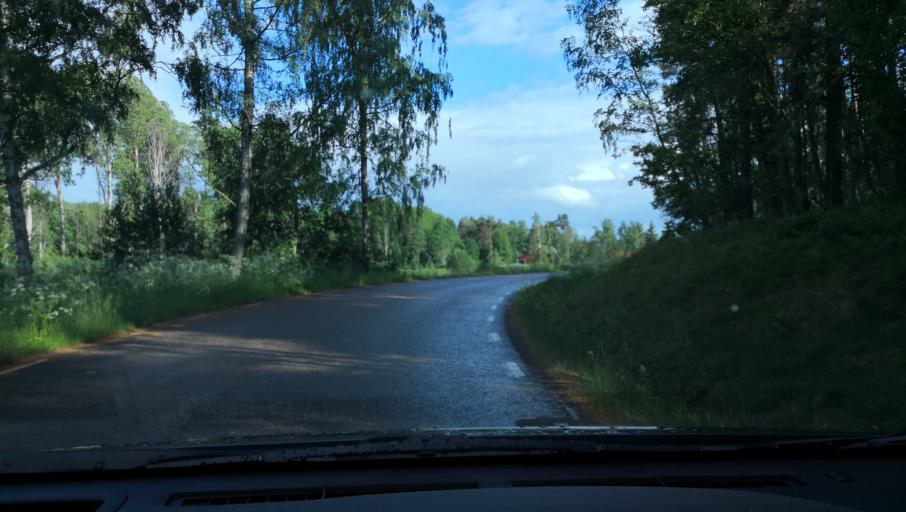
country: SE
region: OErebro
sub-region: Lindesbergs Kommun
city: Fellingsbro
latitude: 59.3011
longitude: 15.6812
